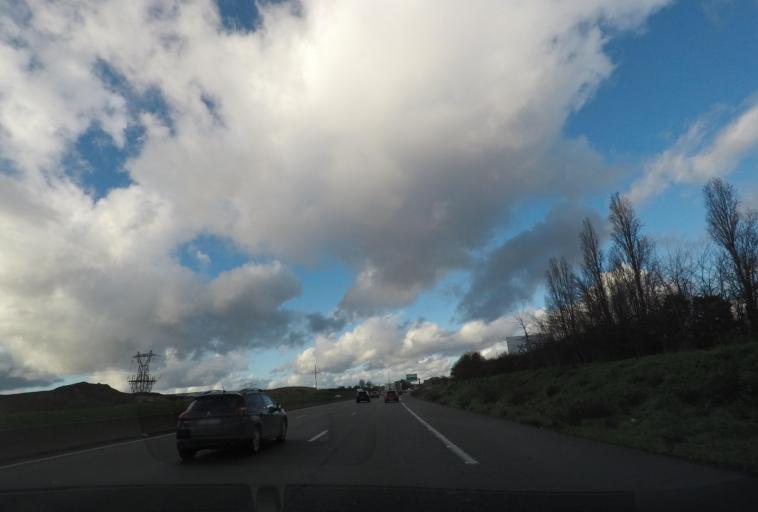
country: FR
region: Ile-de-France
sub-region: Departement de l'Essonne
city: Ormoy
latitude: 48.5673
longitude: 2.4729
